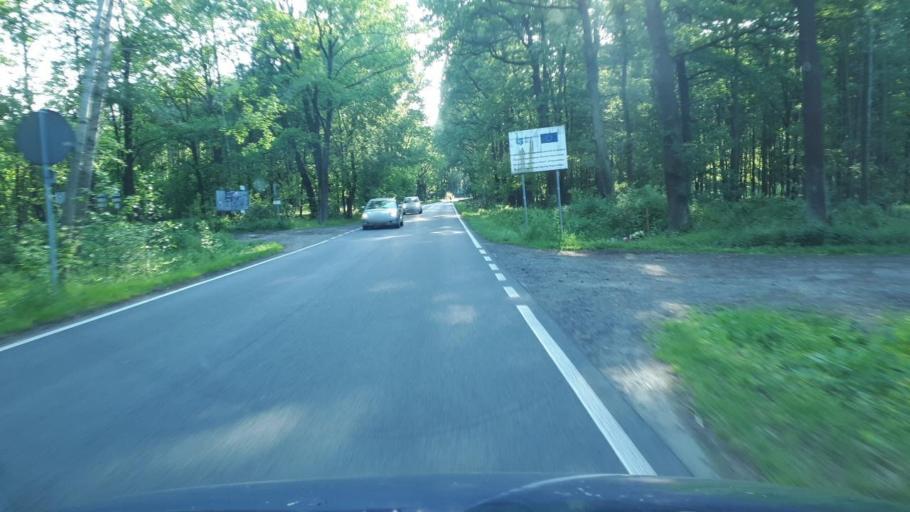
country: PL
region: Silesian Voivodeship
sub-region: Powiat cieszynski
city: Chybie
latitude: 49.8870
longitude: 18.8615
